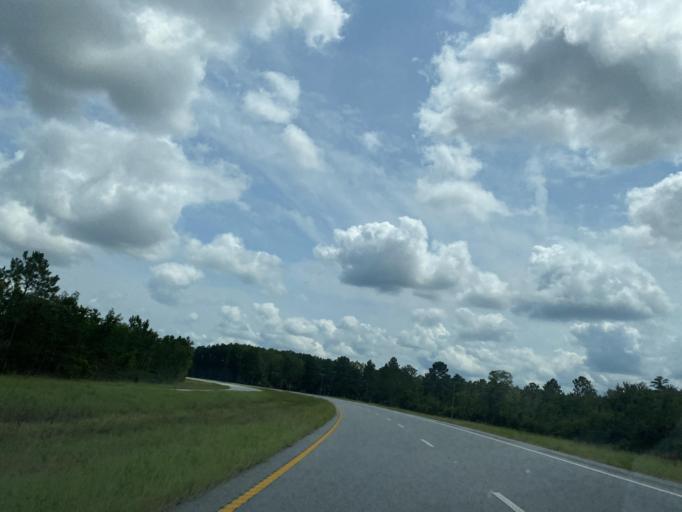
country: US
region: Georgia
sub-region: Ware County
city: Deenwood
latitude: 31.2786
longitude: -82.4511
